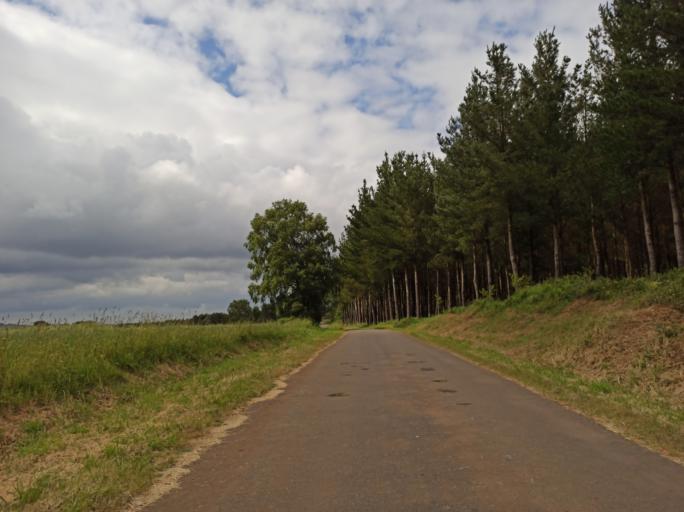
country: ES
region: Galicia
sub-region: Provincia de Pontevedra
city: Silleda
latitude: 42.7621
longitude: -8.1601
